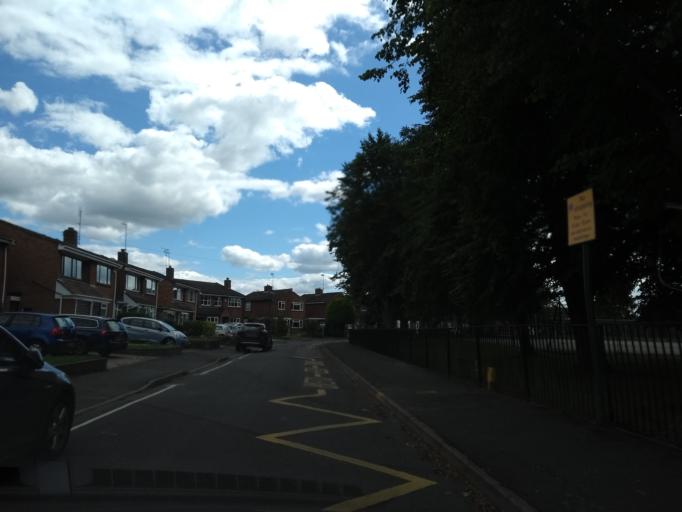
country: GB
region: England
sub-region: Warwickshire
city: Alcester
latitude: 52.2205
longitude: -1.8563
